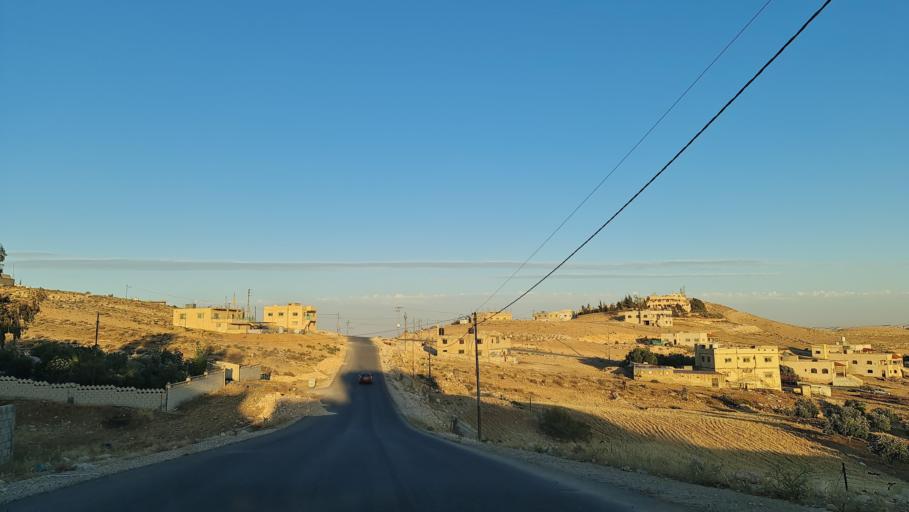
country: JO
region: Zarqa
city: Zarqa
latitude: 32.0886
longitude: 36.0206
